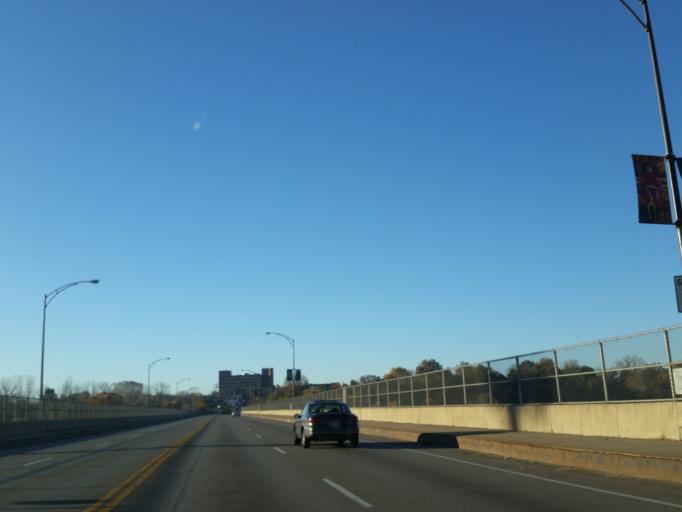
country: US
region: Ohio
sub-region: Cuyahoga County
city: Brooklyn Heights
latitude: 41.4476
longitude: -81.7025
